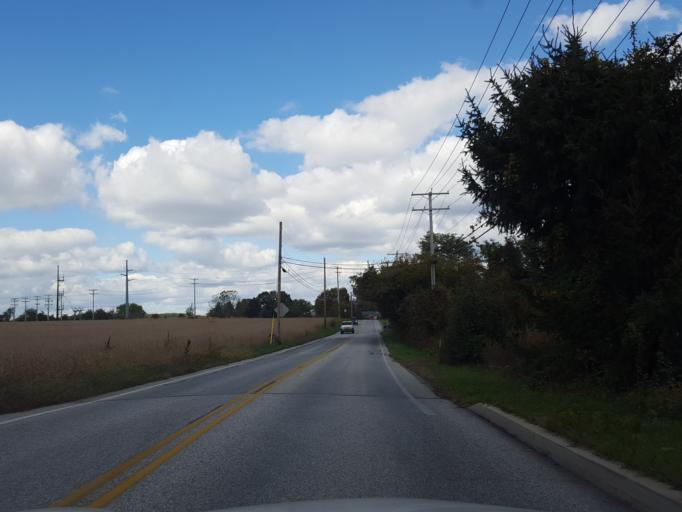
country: US
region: Pennsylvania
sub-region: York County
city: Spry
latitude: 39.9315
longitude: -76.6623
